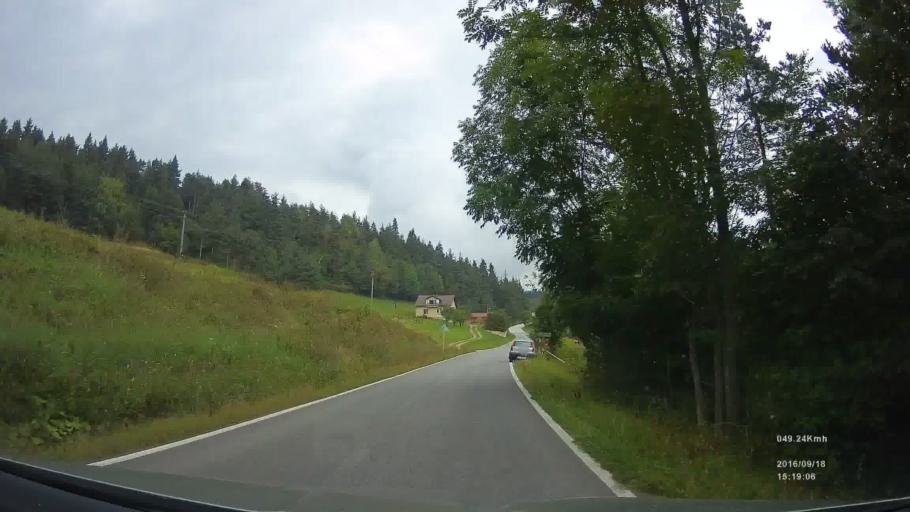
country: SK
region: Presovsky
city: Lubica
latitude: 49.0354
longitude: 20.4897
